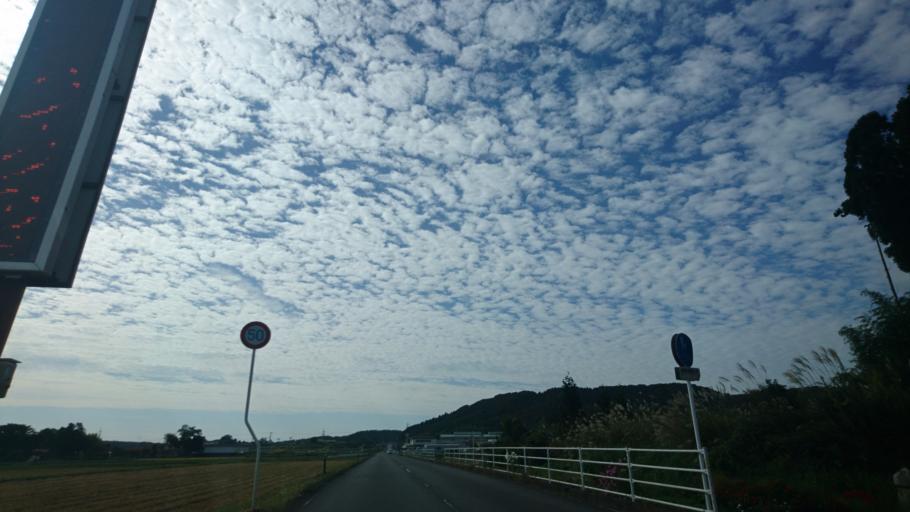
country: JP
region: Fukushima
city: Sukagawa
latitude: 37.3232
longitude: 140.2672
